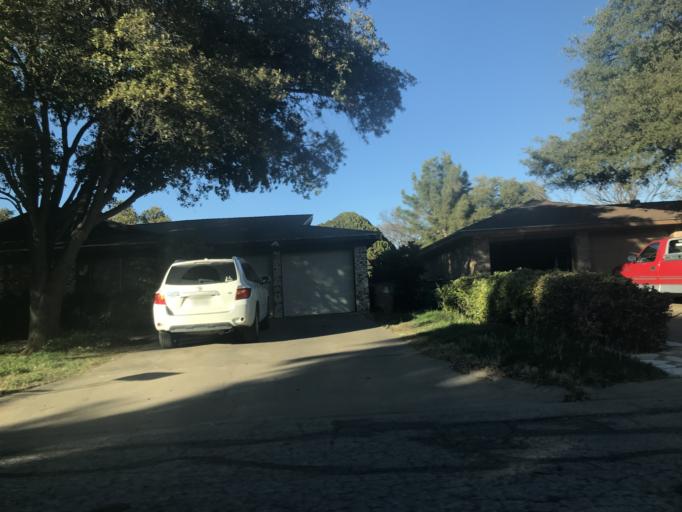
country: US
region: Texas
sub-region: Tom Green County
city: San Angelo
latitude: 31.4297
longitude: -100.4912
